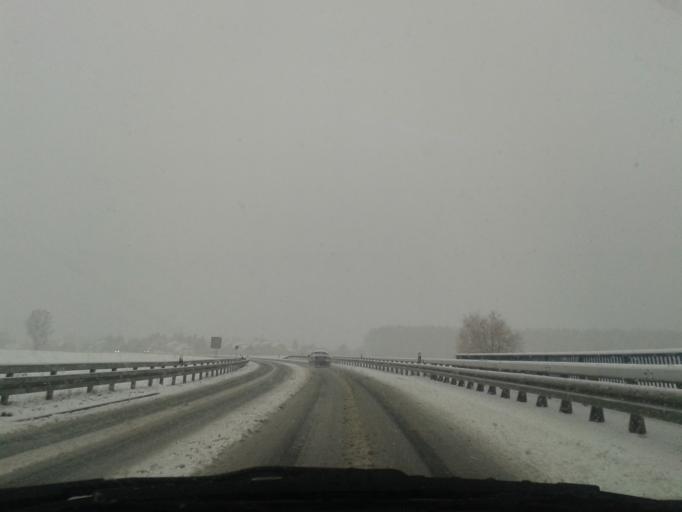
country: DE
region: Saxony
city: Rammenau
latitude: 51.1482
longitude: 14.1548
